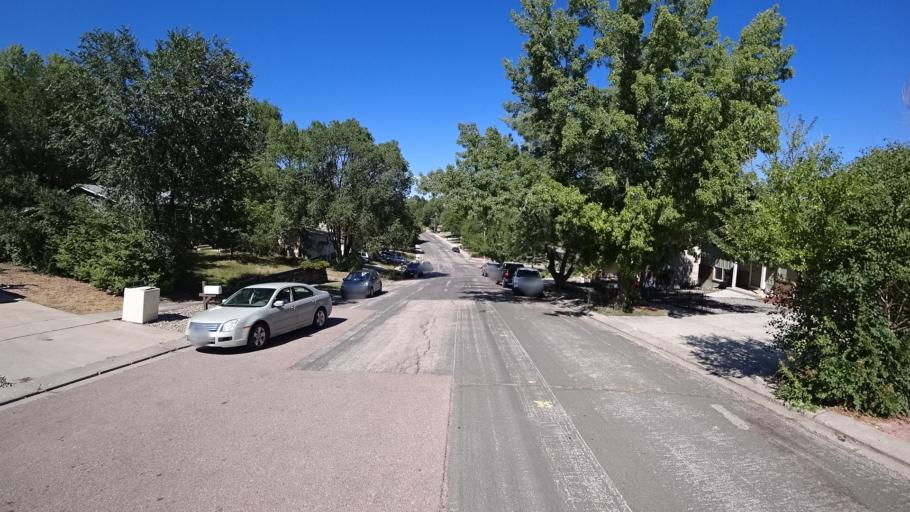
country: US
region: Colorado
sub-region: El Paso County
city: Colorado Springs
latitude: 38.8598
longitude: -104.8598
